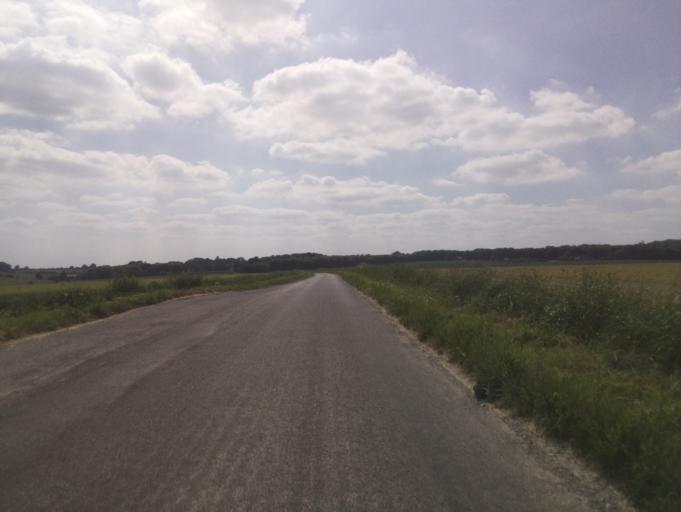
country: GB
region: England
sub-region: Wiltshire
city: Collingbourne Kingston
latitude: 51.2822
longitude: -1.6907
